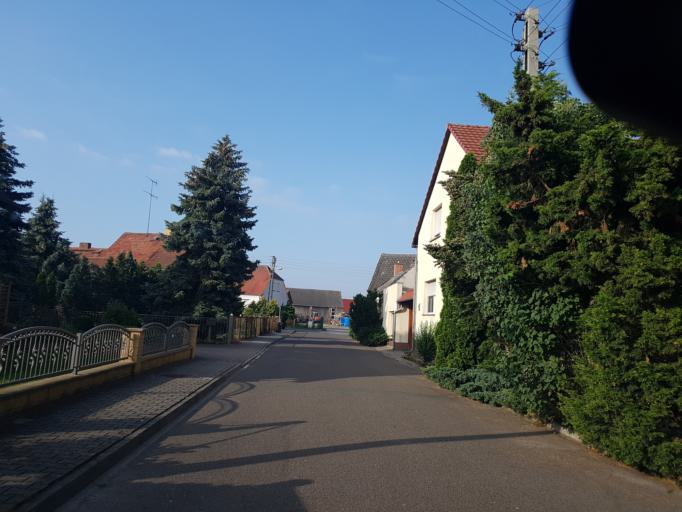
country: DE
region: Saxony-Anhalt
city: Holzdorf
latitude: 51.8568
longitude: 13.1013
